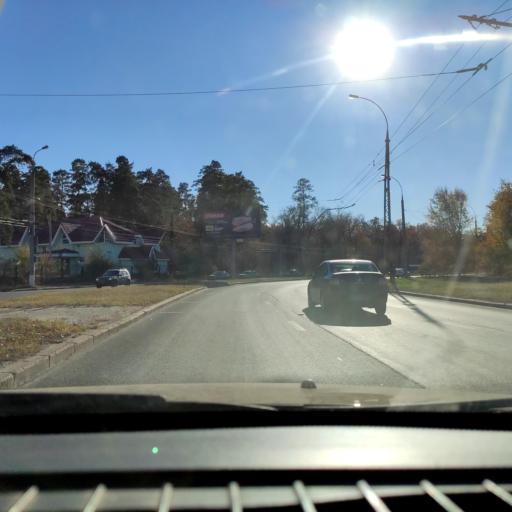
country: RU
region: Samara
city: Tol'yatti
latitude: 53.4993
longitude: 49.2983
